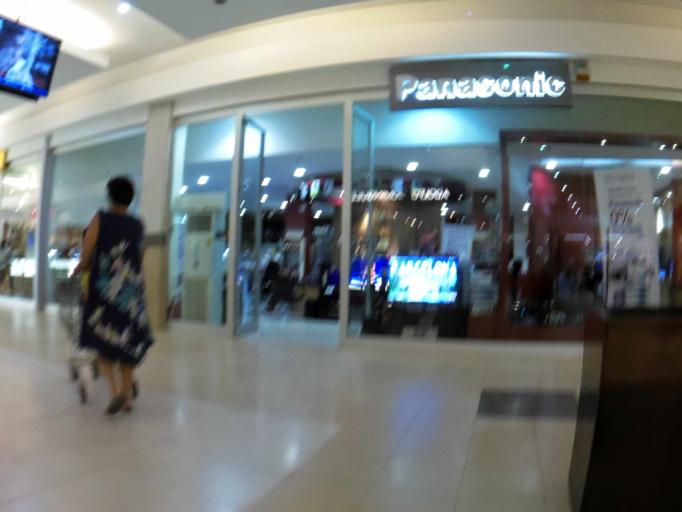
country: GH
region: Greater Accra
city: Medina Estates
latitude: 5.6223
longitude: -0.1727
